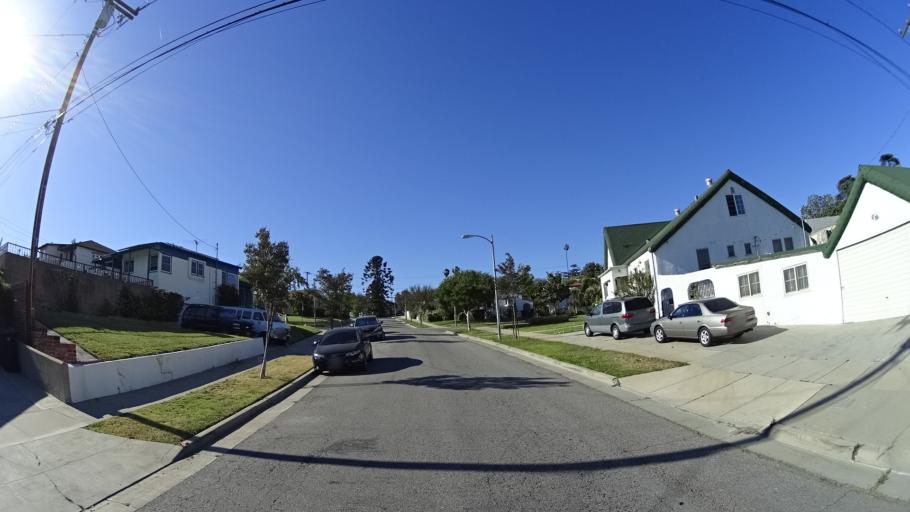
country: US
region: California
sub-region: Los Angeles County
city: Belvedere
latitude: 34.0701
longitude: -118.1558
